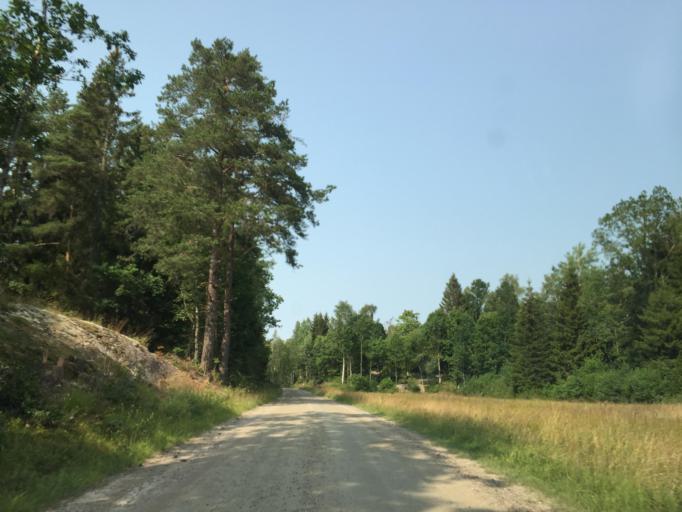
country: SE
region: Vaestra Goetaland
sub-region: Lilla Edets Kommun
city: Lilla Edet
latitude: 58.2598
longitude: 12.0973
